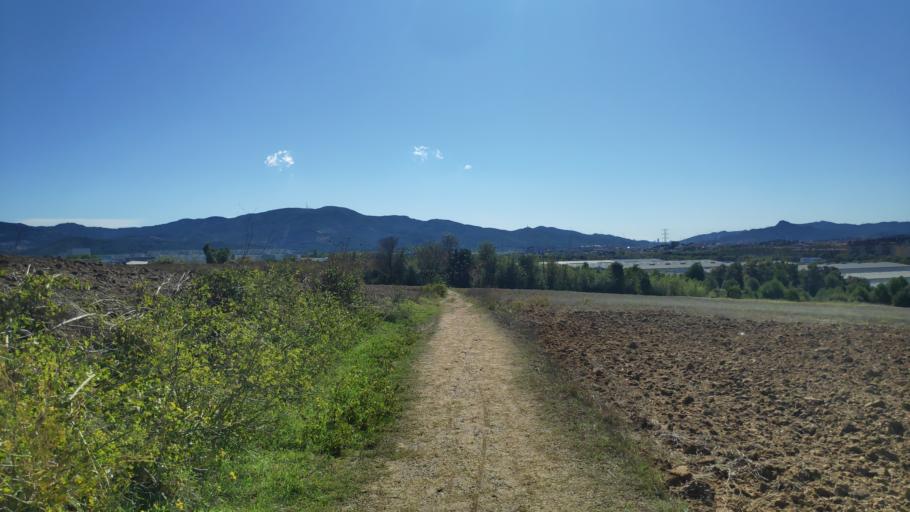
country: ES
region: Catalonia
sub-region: Provincia de Barcelona
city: Santa Perpetua de Mogoda
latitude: 41.5407
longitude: 2.1916
